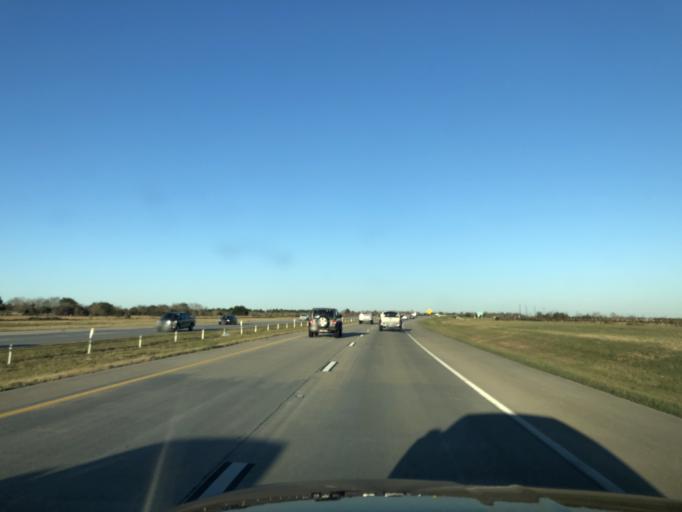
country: US
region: Texas
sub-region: Harris County
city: Cypress
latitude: 30.0486
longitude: -95.7518
